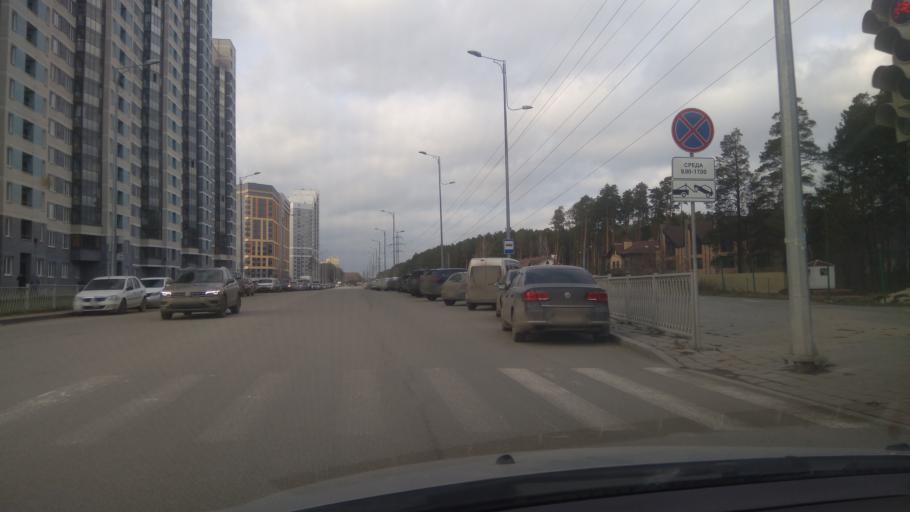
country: RU
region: Sverdlovsk
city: Sovkhoznyy
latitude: 56.7828
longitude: 60.5545
